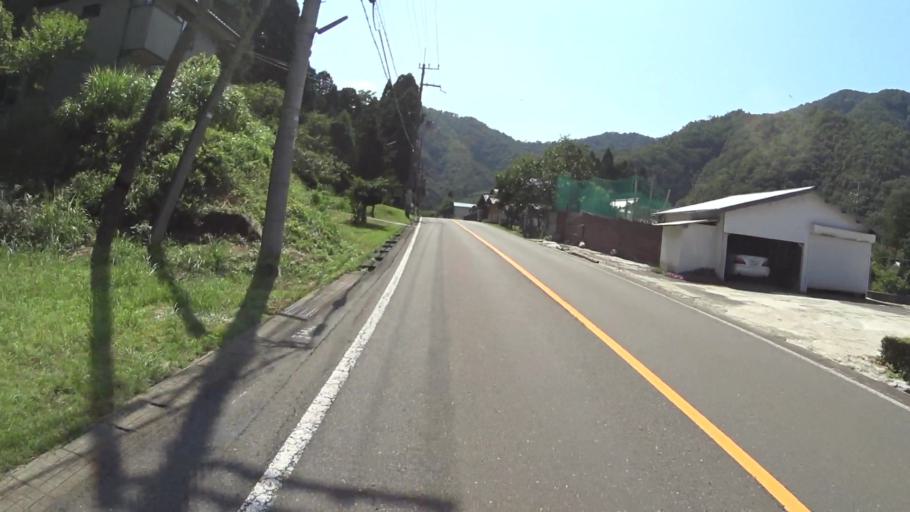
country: JP
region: Fukui
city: Obama
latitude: 35.4370
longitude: 135.6963
